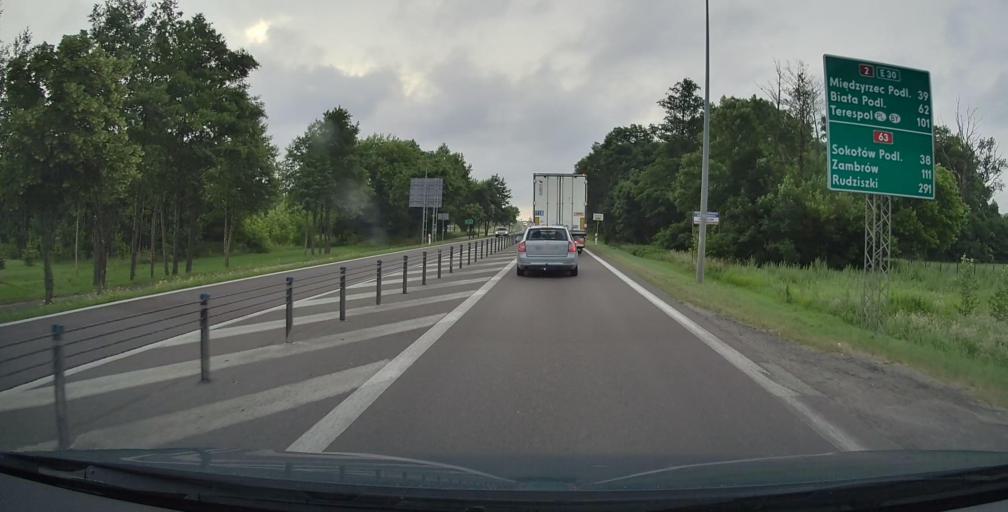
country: PL
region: Masovian Voivodeship
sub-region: Siedlce
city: Siedlce
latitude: 52.1325
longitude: 22.2943
